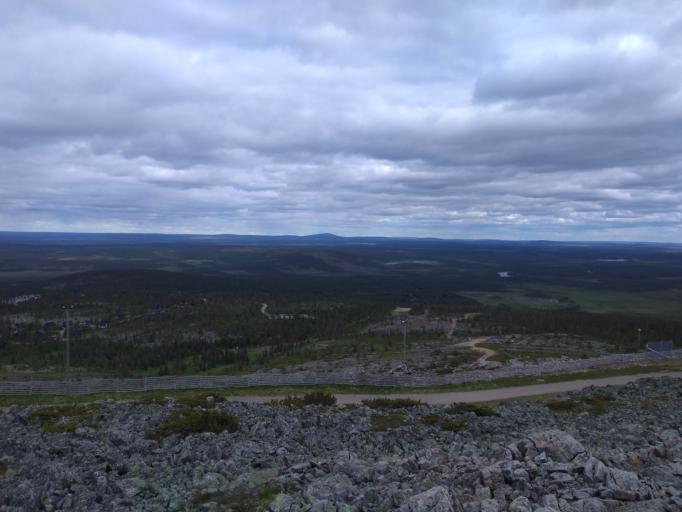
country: FI
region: Lapland
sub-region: Tunturi-Lappi
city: Kittilae
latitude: 67.7836
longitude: 24.8582
